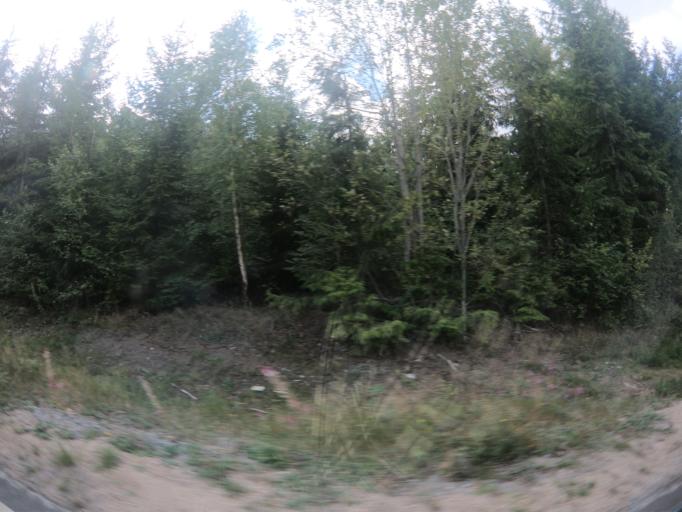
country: SE
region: Kronoberg
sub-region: Vaxjo Kommun
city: Braas
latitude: 57.1873
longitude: 14.9602
